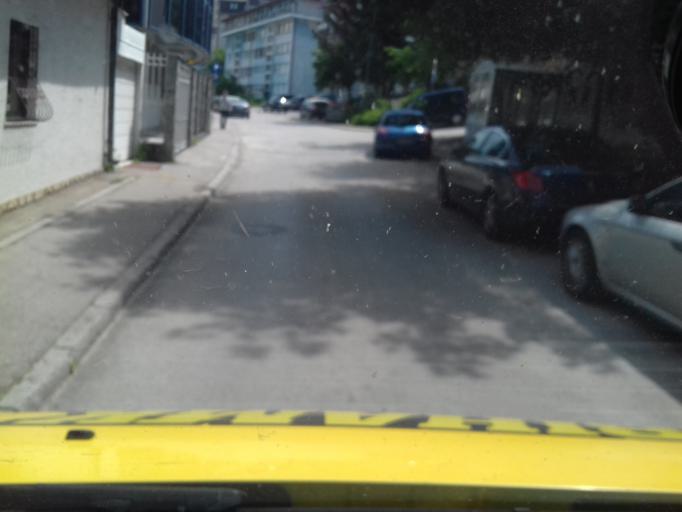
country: BA
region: Federation of Bosnia and Herzegovina
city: Kobilja Glava
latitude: 43.8488
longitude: 18.3986
